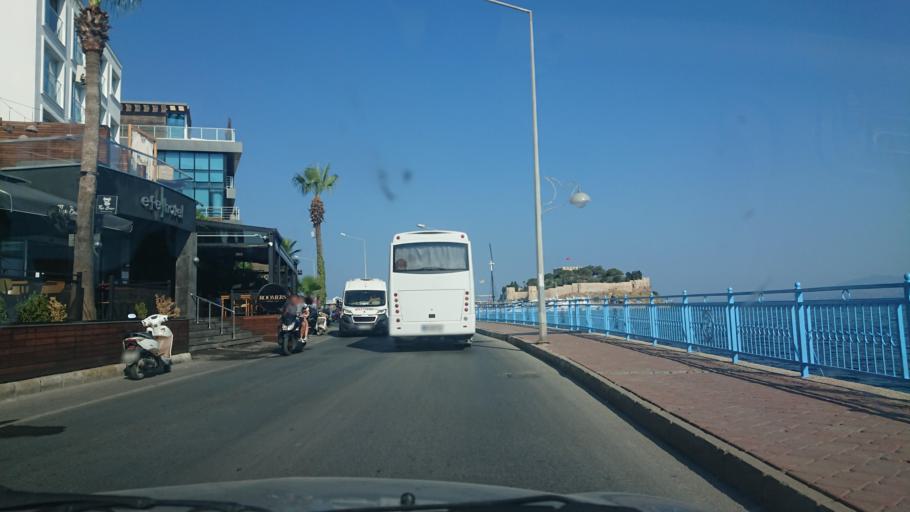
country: TR
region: Aydin
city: Kusadasi
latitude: 37.8612
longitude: 27.2521
